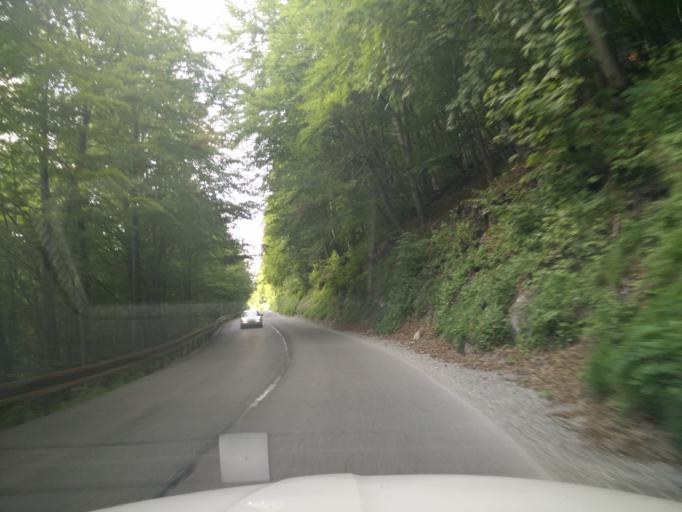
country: SK
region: Zilinsky
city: Rajec
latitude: 48.9549
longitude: 18.6190
